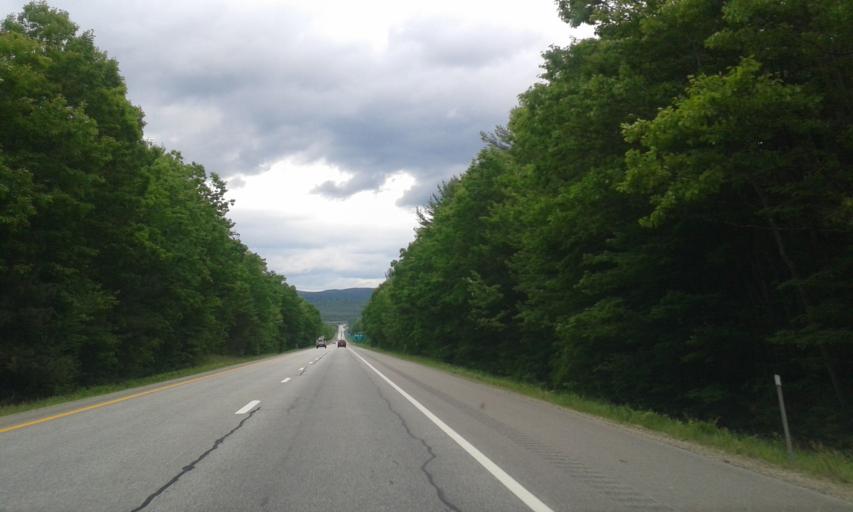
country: US
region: New Hampshire
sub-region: Belknap County
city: Sanbornton
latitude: 43.4751
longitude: -71.5870
